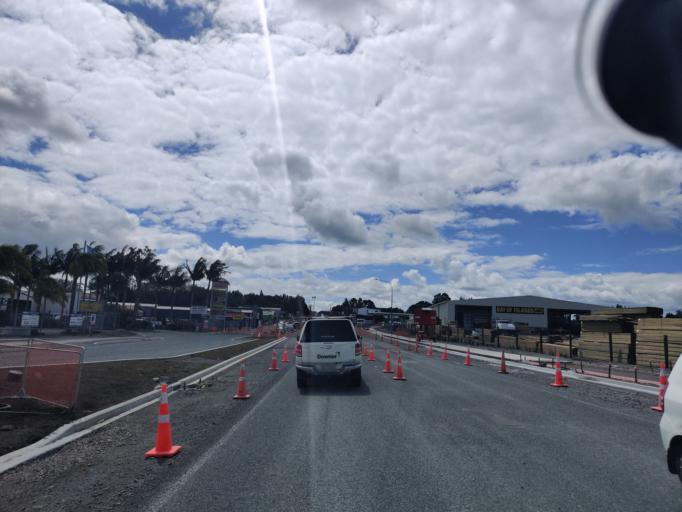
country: NZ
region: Northland
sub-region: Far North District
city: Kerikeri
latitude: -35.2079
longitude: 173.9192
